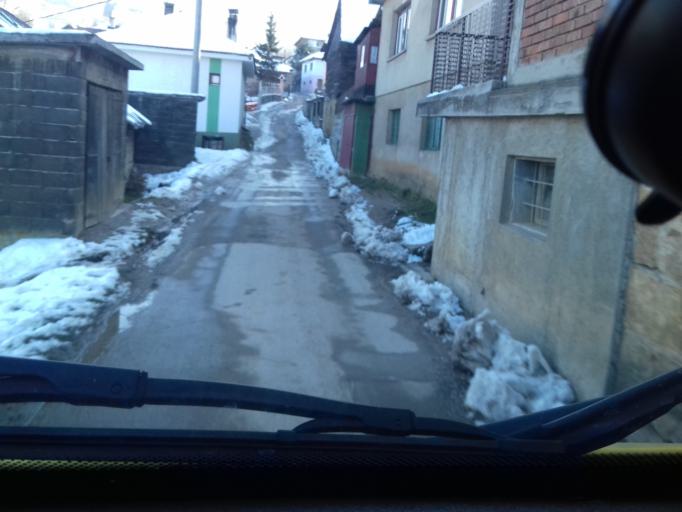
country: BA
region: Federation of Bosnia and Herzegovina
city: Zenica
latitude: 44.1782
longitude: 17.8805
